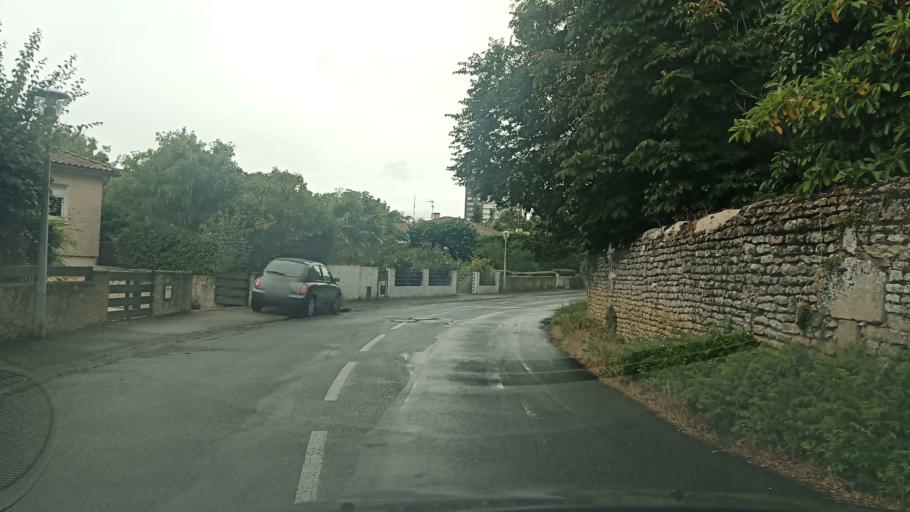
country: FR
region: Poitou-Charentes
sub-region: Departement de la Vienne
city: Poitiers
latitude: 46.5926
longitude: 0.3707
